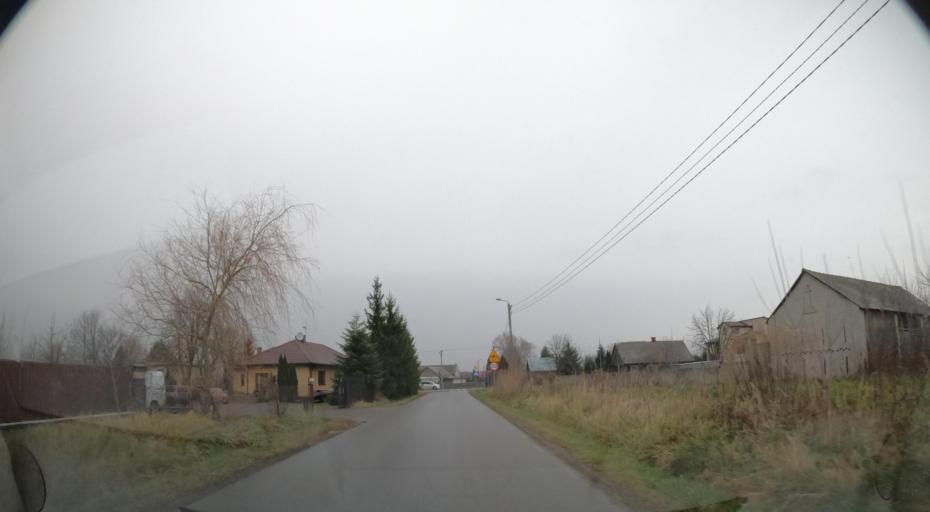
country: PL
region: Masovian Voivodeship
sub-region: Radom
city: Radom
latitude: 51.4155
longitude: 21.2225
